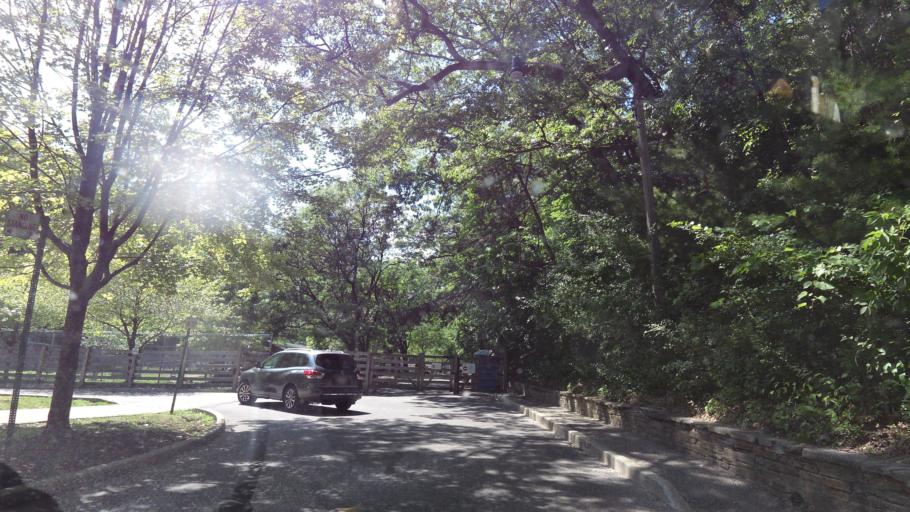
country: CA
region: Ontario
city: Toronto
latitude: 43.6428
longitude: -79.4604
